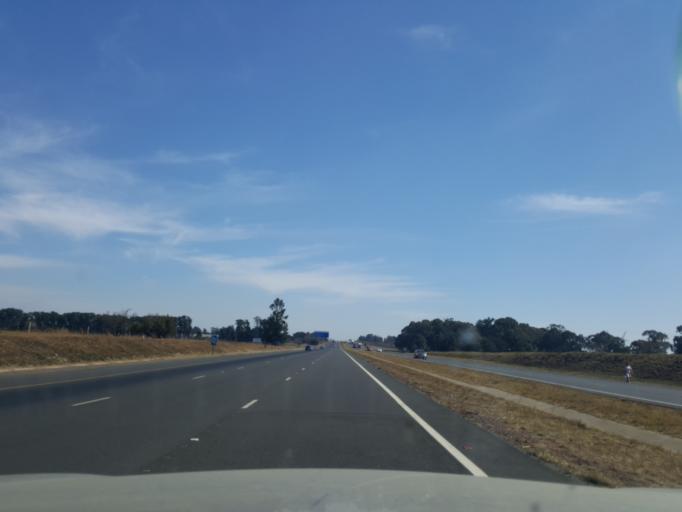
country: ZA
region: Mpumalanga
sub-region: Nkangala District Municipality
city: Middelburg
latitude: -25.8320
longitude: 29.4694
